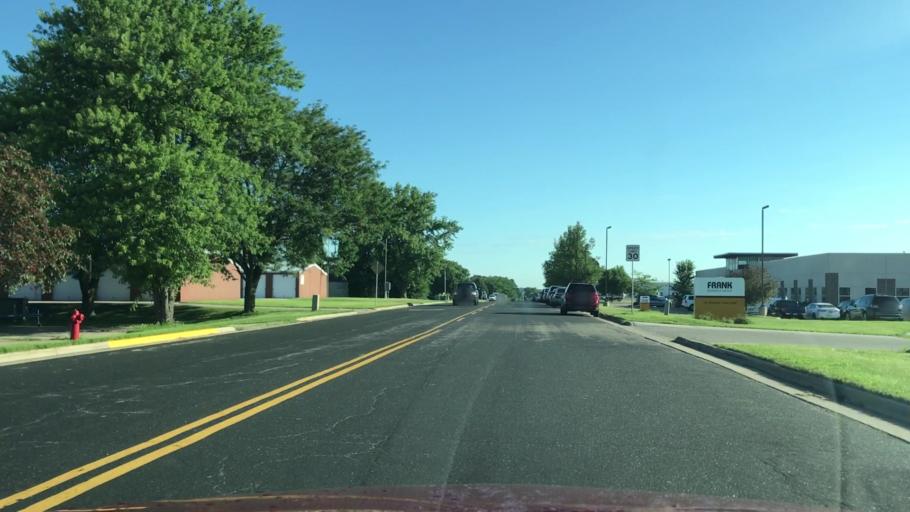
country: US
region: Wisconsin
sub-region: Dane County
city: Middleton
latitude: 43.0982
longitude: -89.5363
